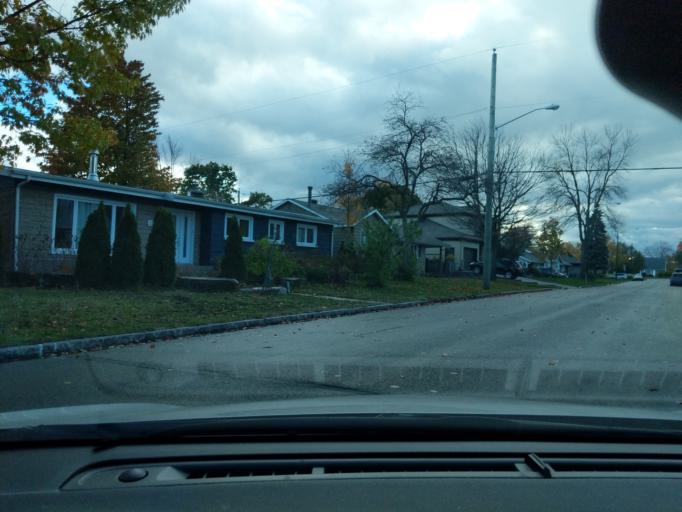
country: CA
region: Quebec
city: L'Ancienne-Lorette
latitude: 46.7638
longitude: -71.2892
